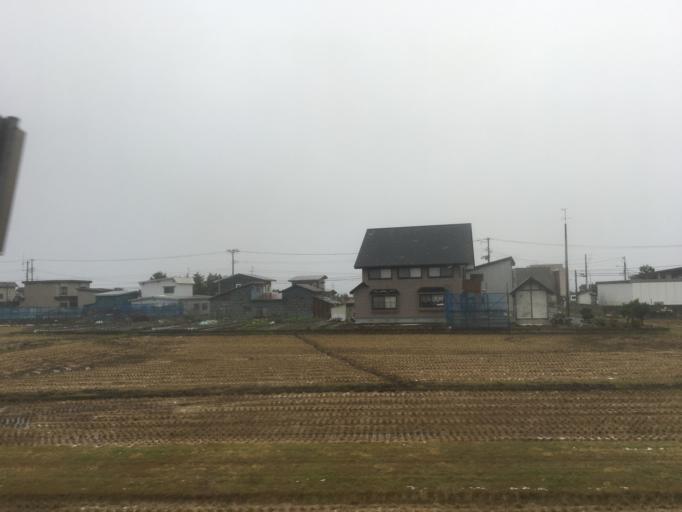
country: JP
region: Aomori
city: Aomori Shi
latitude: 40.9110
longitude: 140.6700
